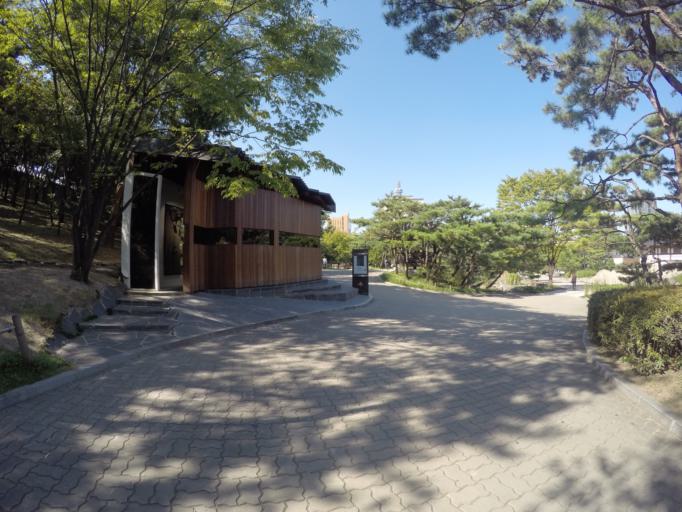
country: KR
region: Seoul
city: Seoul
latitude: 37.5582
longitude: 126.9929
